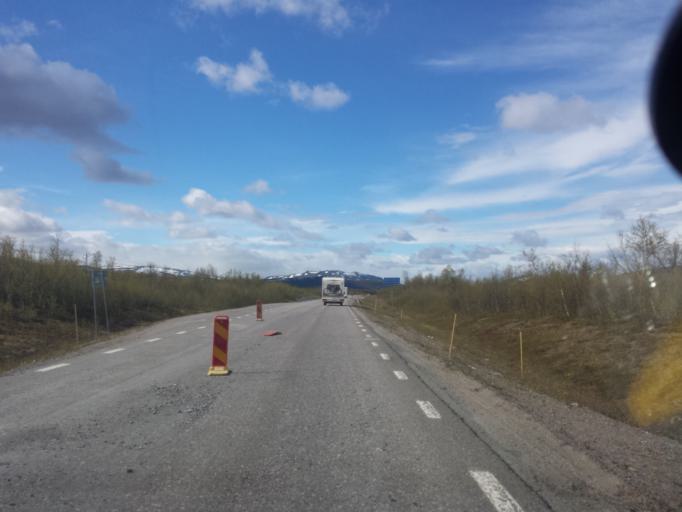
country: SE
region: Norrbotten
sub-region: Kiruna Kommun
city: Kiruna
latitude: 68.0065
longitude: 19.8497
